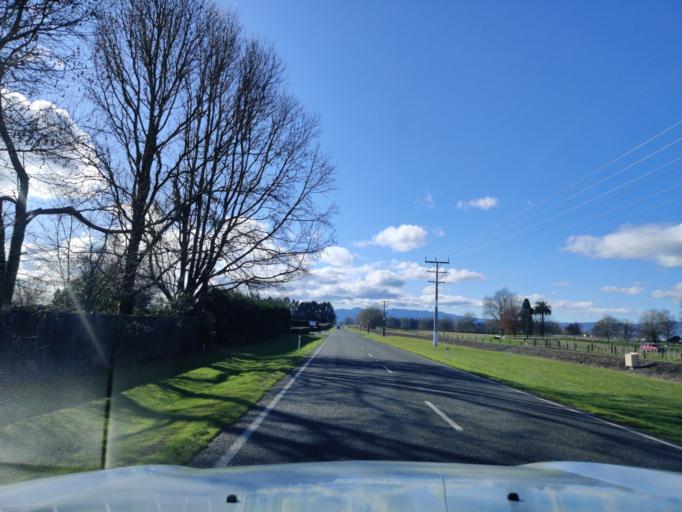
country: NZ
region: Waikato
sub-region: Matamata-Piako District
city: Matamata
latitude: -37.8580
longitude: 175.7561
